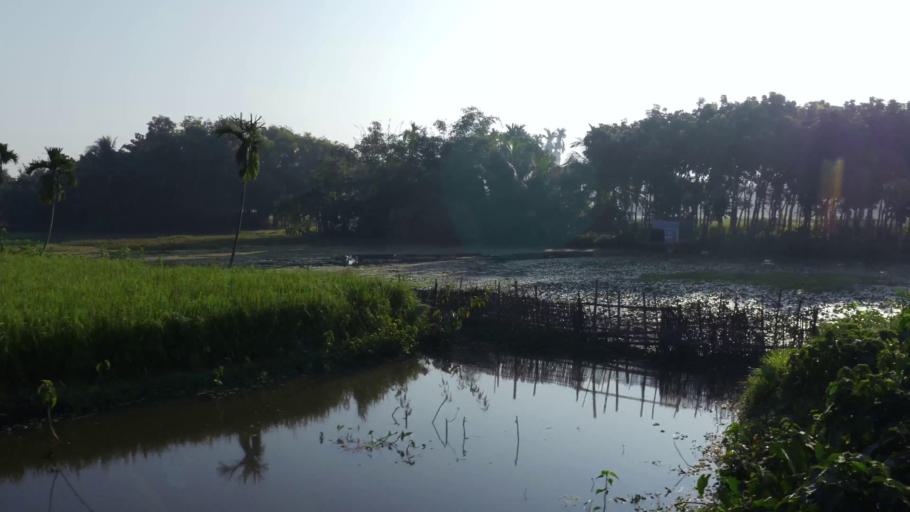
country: BD
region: Dhaka
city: Jamalpur
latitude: 24.9129
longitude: 89.9586
